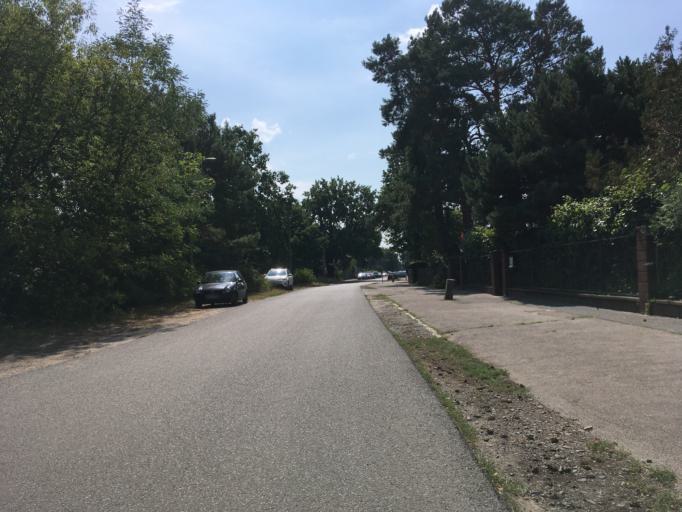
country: DE
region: Berlin
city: Mahlsdorf
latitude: 52.4831
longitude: 13.6108
